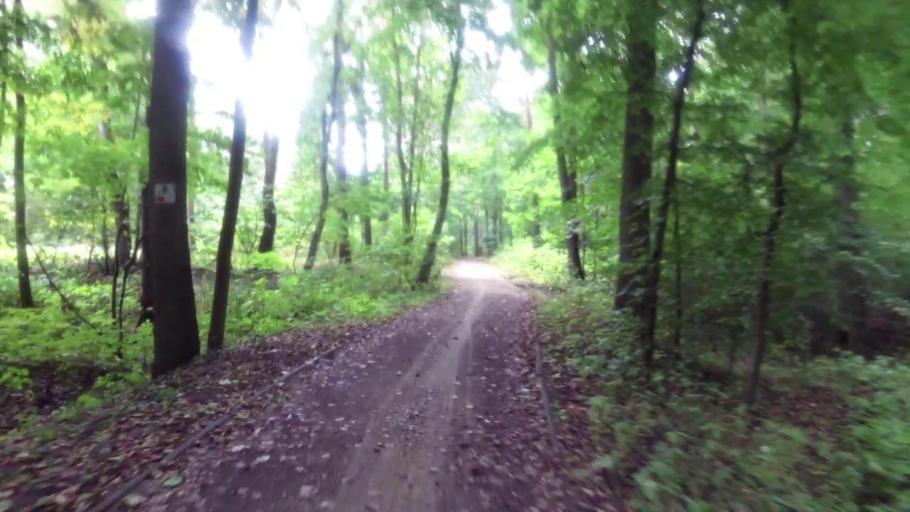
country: PL
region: West Pomeranian Voivodeship
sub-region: Powiat mysliborski
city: Debno
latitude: 52.7138
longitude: 14.6929
